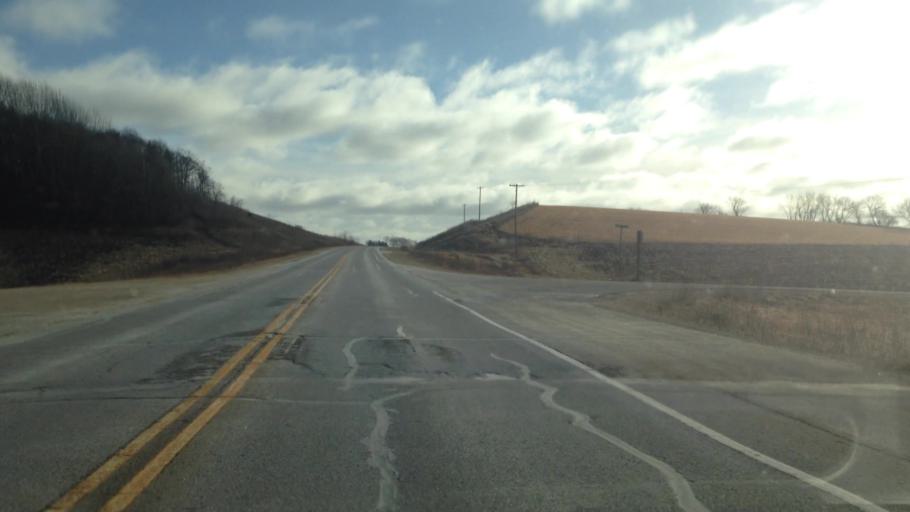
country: US
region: Wisconsin
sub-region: Dodge County
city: Theresa
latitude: 43.4335
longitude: -88.4606
